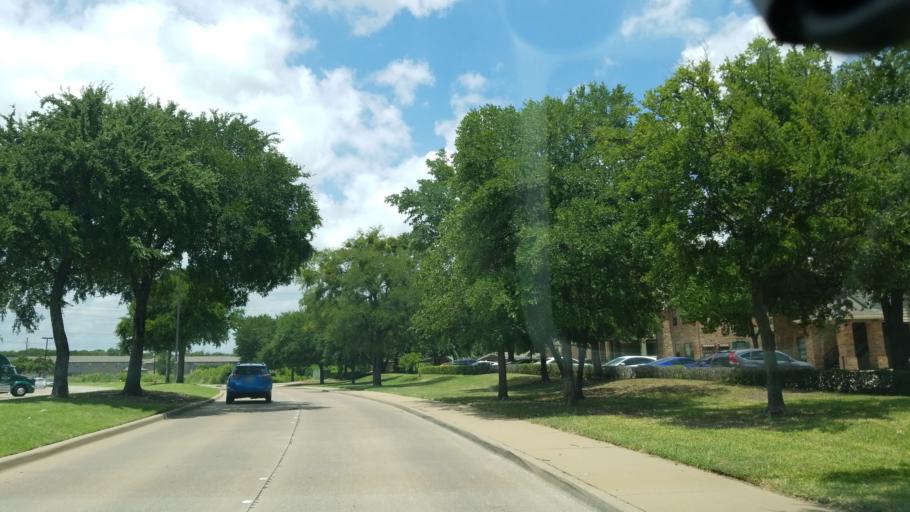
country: US
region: Texas
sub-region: Dallas County
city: Coppell
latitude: 32.9570
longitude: -96.9568
